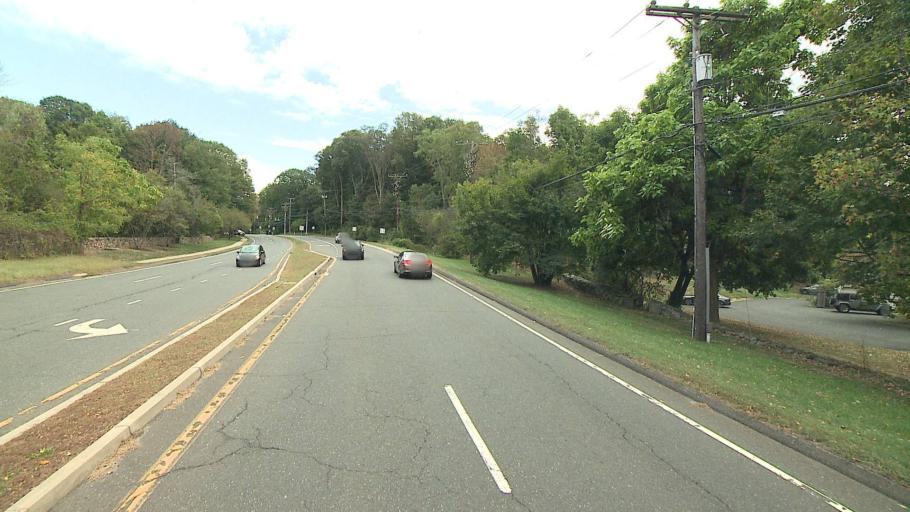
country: US
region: Connecticut
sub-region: Fairfield County
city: Wilton
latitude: 41.1811
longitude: -73.4152
